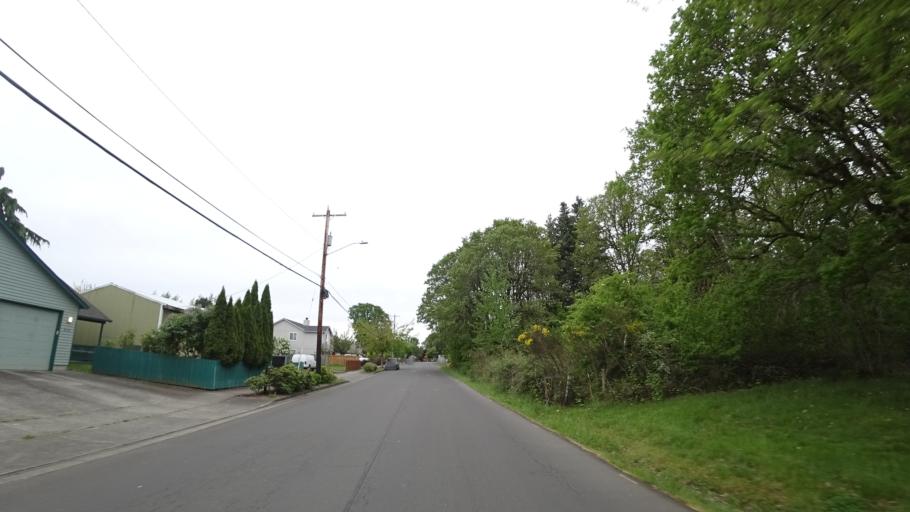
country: US
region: Oregon
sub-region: Washington County
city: Aloha
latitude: 45.5139
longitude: -122.9146
